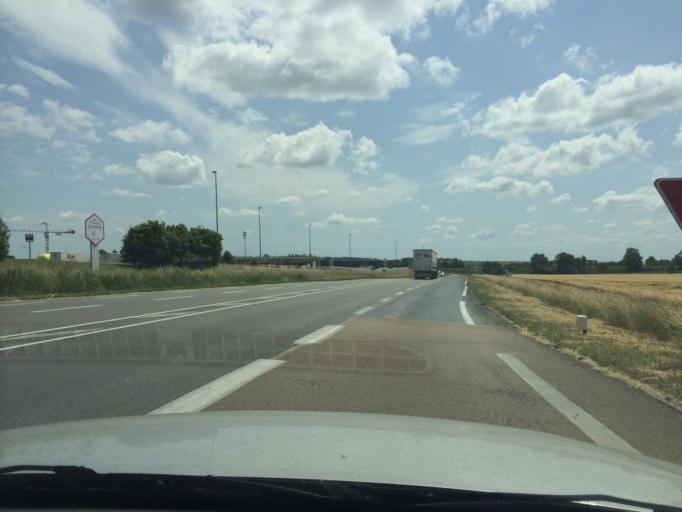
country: FR
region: Champagne-Ardenne
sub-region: Departement de la Marne
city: Fagnieres
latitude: 49.0385
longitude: 4.3217
